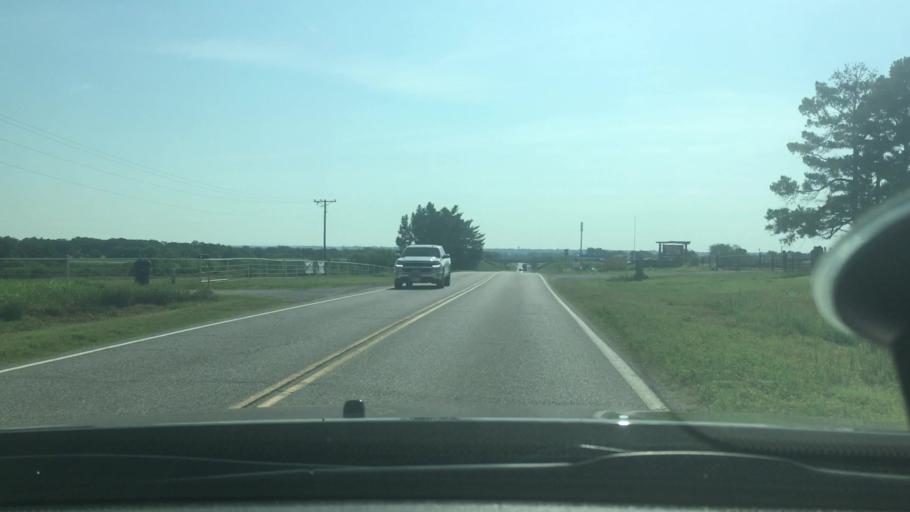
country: US
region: Oklahoma
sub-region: Garvin County
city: Wynnewood
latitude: 34.6517
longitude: -97.2260
